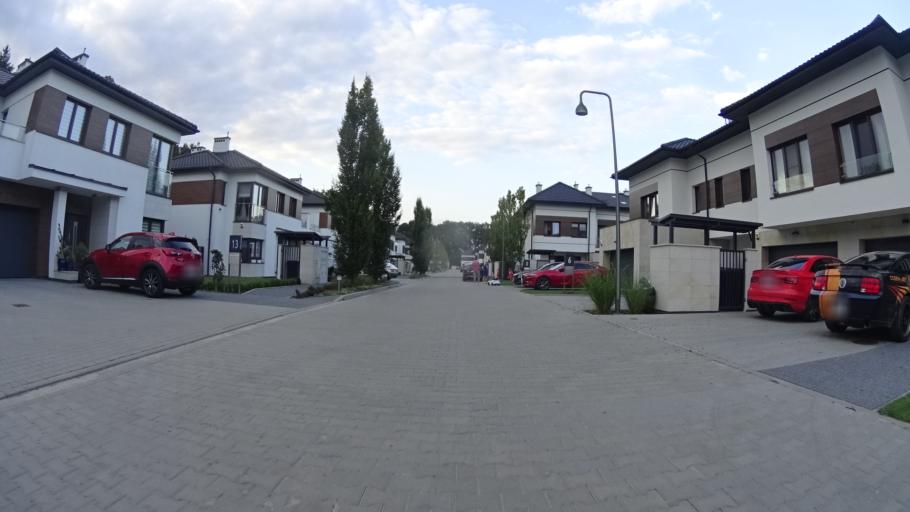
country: PL
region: Masovian Voivodeship
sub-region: Powiat warszawski zachodni
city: Ozarow Mazowiecki
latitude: 52.2320
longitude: 20.8057
